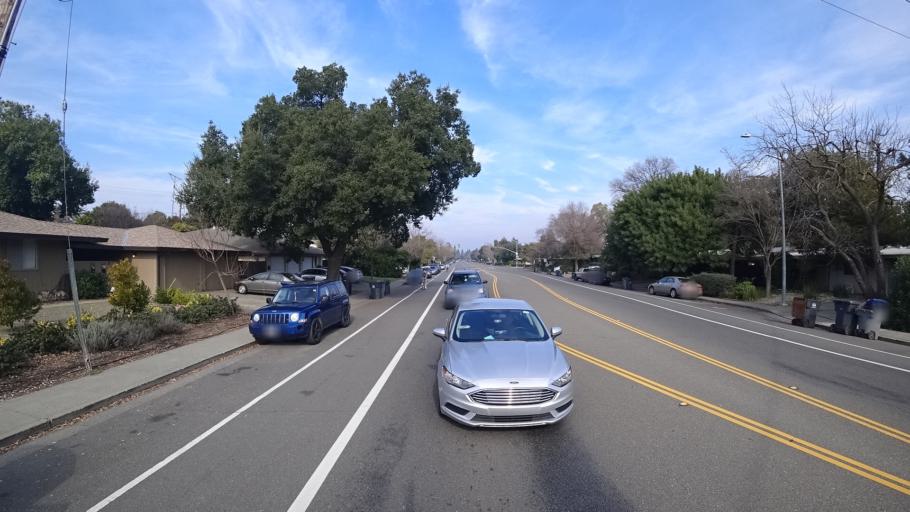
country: US
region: California
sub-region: Yolo County
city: Davis
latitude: 38.5551
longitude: -121.7587
